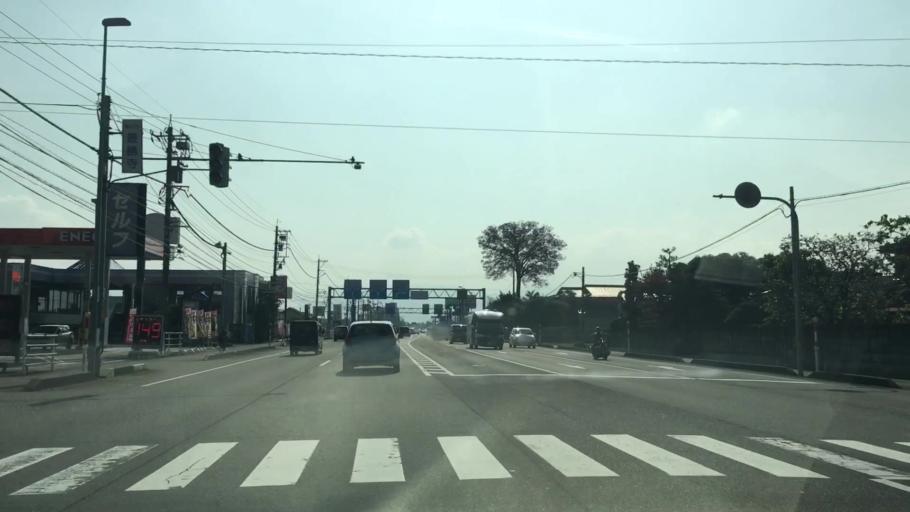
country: JP
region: Toyama
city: Toyama-shi
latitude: 36.6450
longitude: 137.2096
